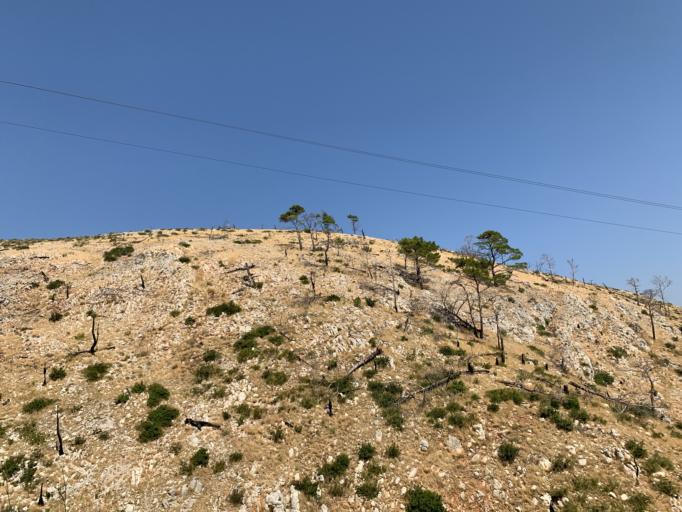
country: GR
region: North Aegean
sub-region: Chios
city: Thymiana
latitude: 38.3138
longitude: 26.0050
